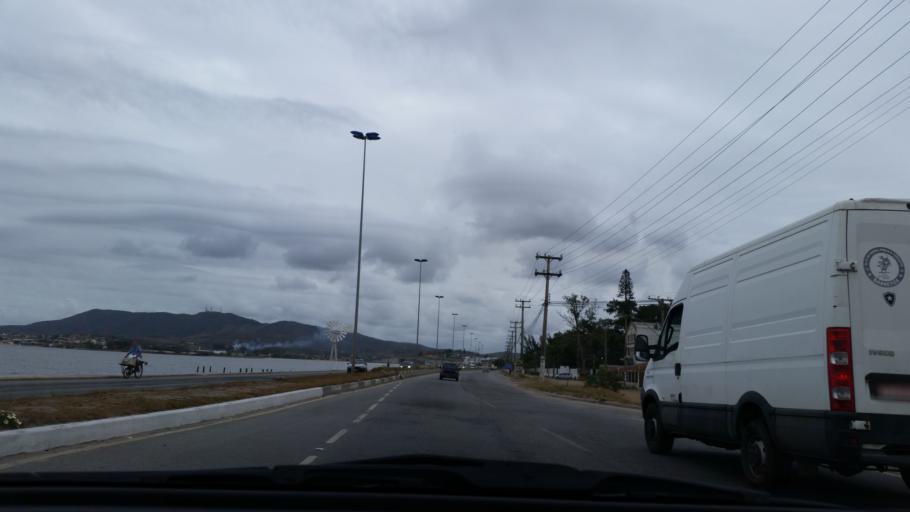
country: BR
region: Rio de Janeiro
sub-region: Sao Pedro Da Aldeia
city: Sao Pedro da Aldeia
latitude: -22.8313
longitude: -42.1068
